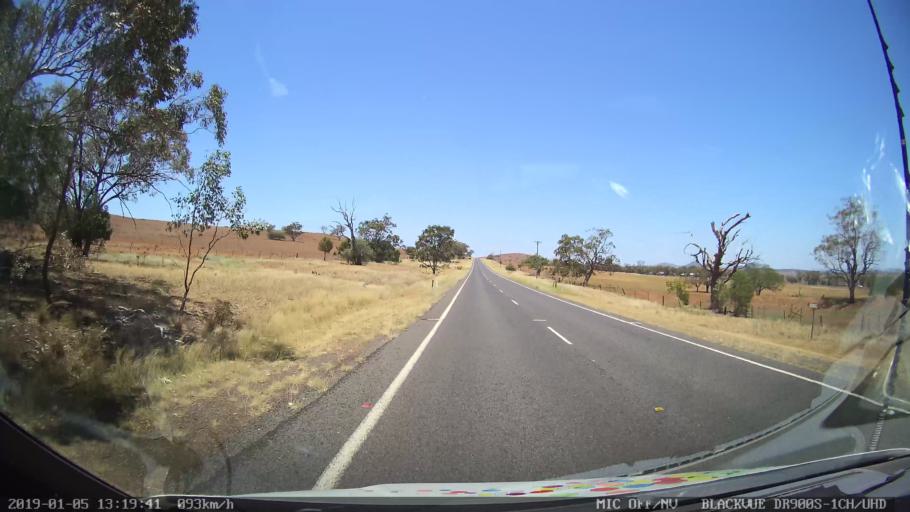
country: AU
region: New South Wales
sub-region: Gunnedah
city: Gunnedah
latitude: -31.0984
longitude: 149.9237
